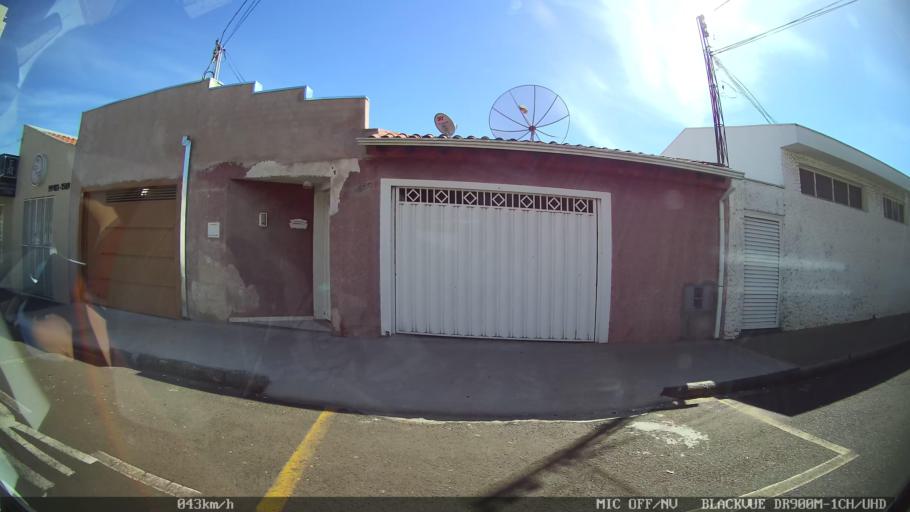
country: BR
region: Sao Paulo
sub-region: Franca
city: Franca
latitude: -20.5465
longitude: -47.3920
